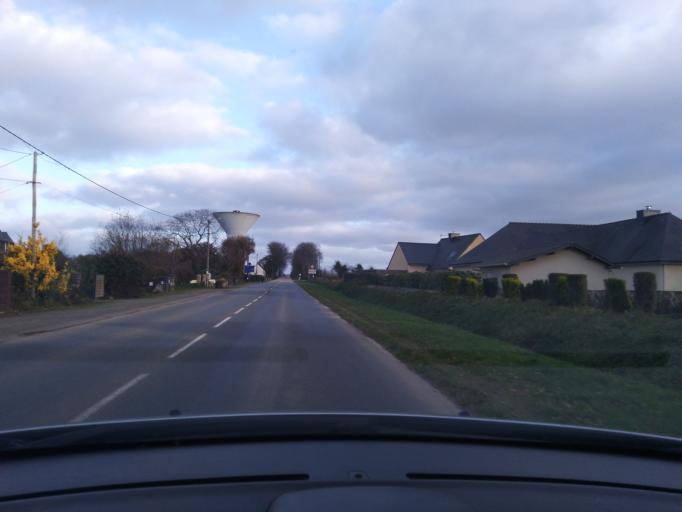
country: FR
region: Brittany
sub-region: Departement du Finistere
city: Plouigneau
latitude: 48.5688
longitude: -3.6926
